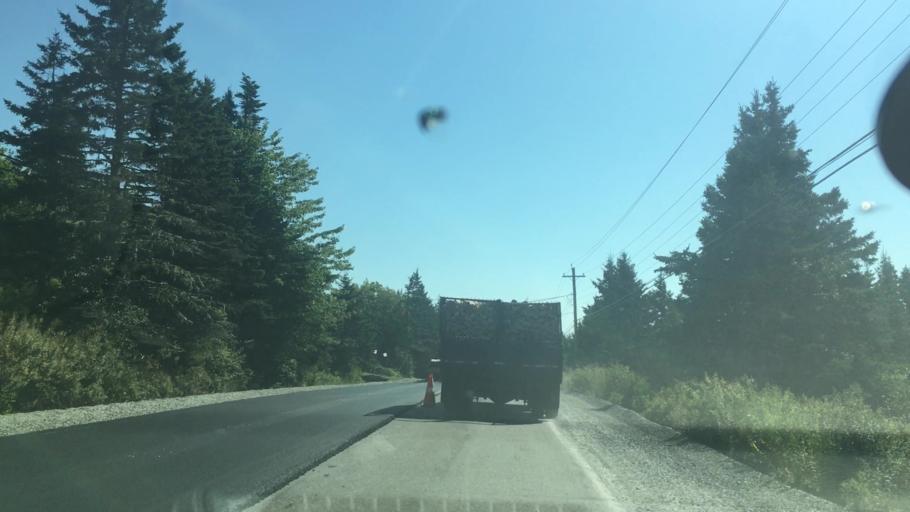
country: CA
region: Nova Scotia
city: New Glasgow
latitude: 44.9089
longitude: -62.5006
